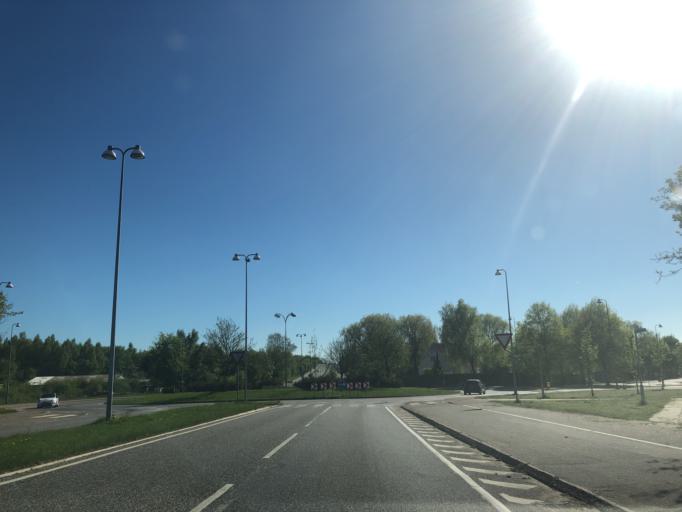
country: DK
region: Zealand
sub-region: Koge Kommune
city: Koge
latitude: 55.4362
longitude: 12.1615
